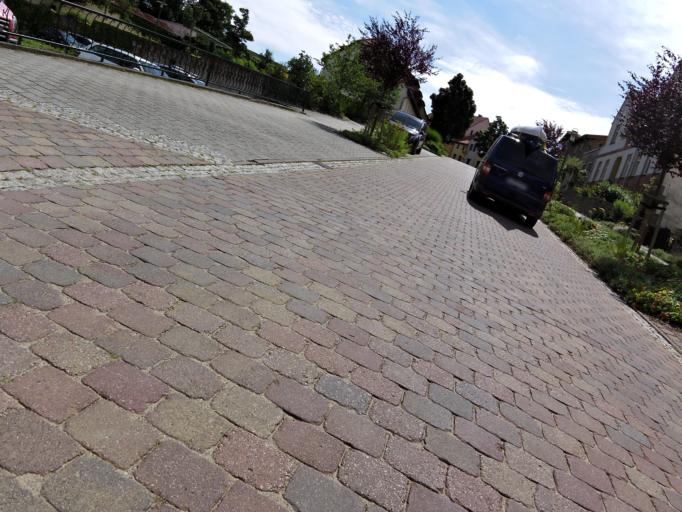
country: DE
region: Mecklenburg-Vorpommern
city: Loitz
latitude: 53.3356
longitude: 13.4351
